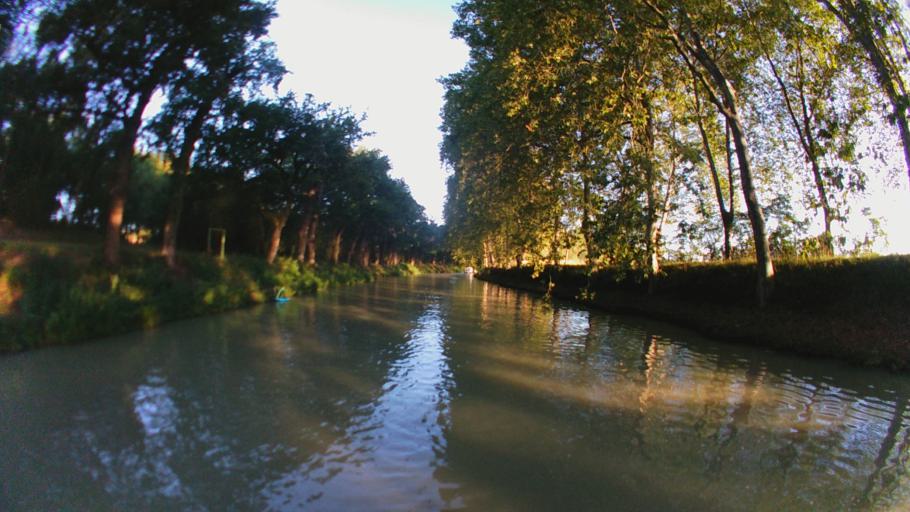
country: FR
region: Midi-Pyrenees
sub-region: Departement de la Haute-Garonne
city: Villenouvelle
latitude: 43.4113
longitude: 1.6497
